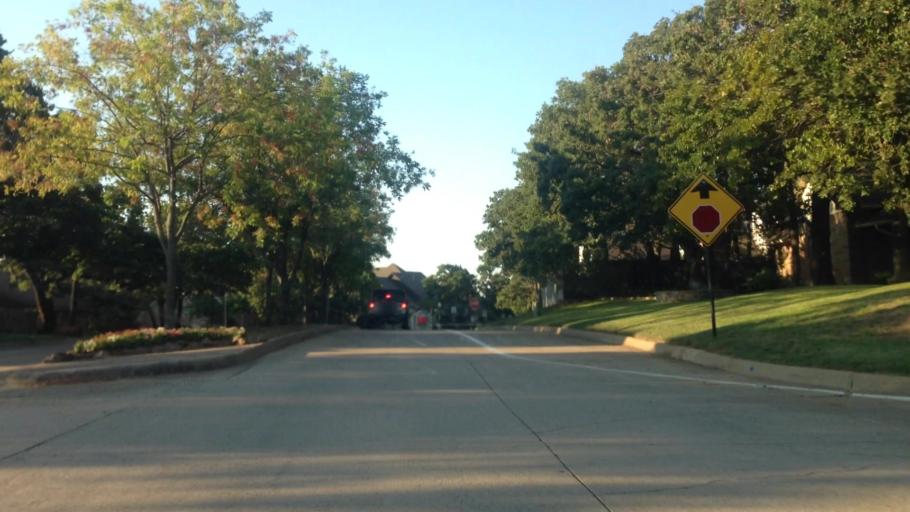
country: US
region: Texas
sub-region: Denton County
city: Trophy Club
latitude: 32.9903
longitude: -97.1692
